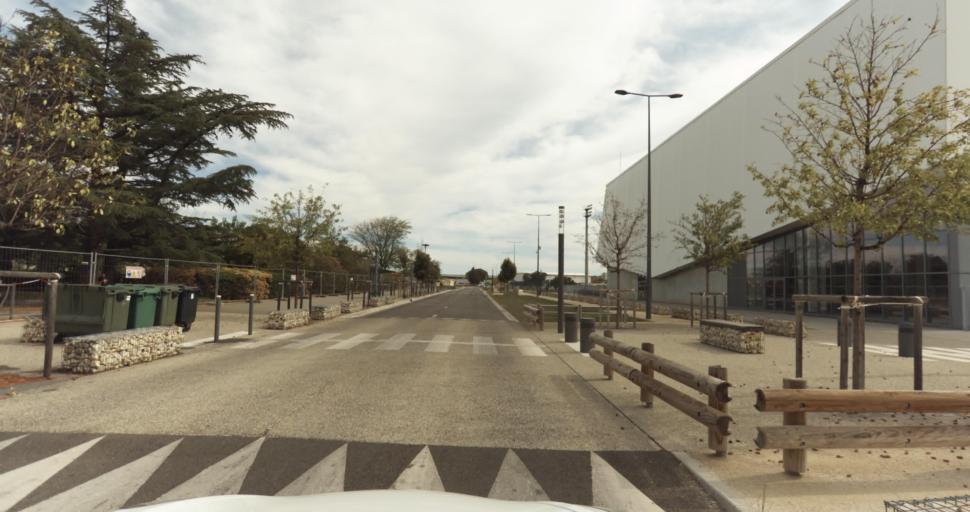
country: FR
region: Provence-Alpes-Cote d'Azur
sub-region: Departement des Bouches-du-Rhone
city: Miramas
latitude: 43.5943
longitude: 4.9980
